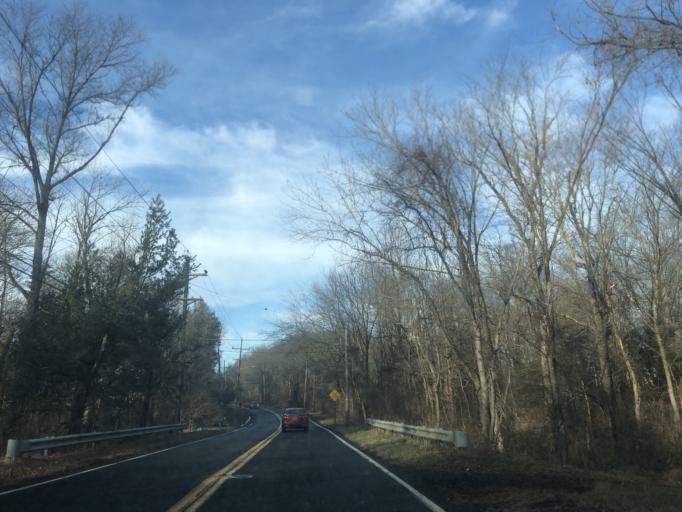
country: US
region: New Jersey
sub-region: Somerset County
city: Kingston
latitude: 40.3809
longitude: -74.5955
